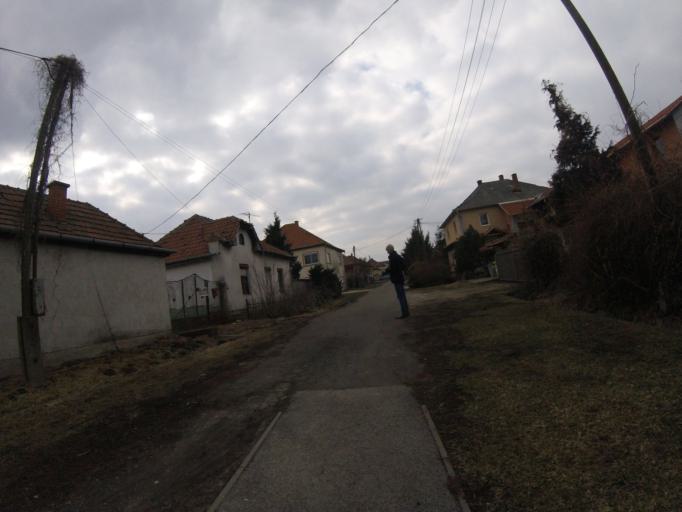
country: HU
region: Heves
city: Egerszalok
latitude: 47.8672
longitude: 20.3220
